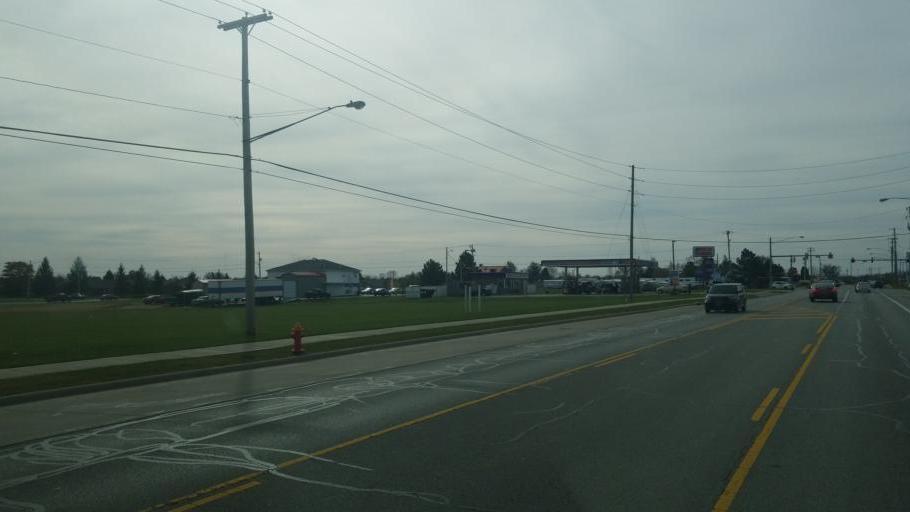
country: US
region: Ohio
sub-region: Madison County
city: London
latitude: 39.9041
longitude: -83.4302
